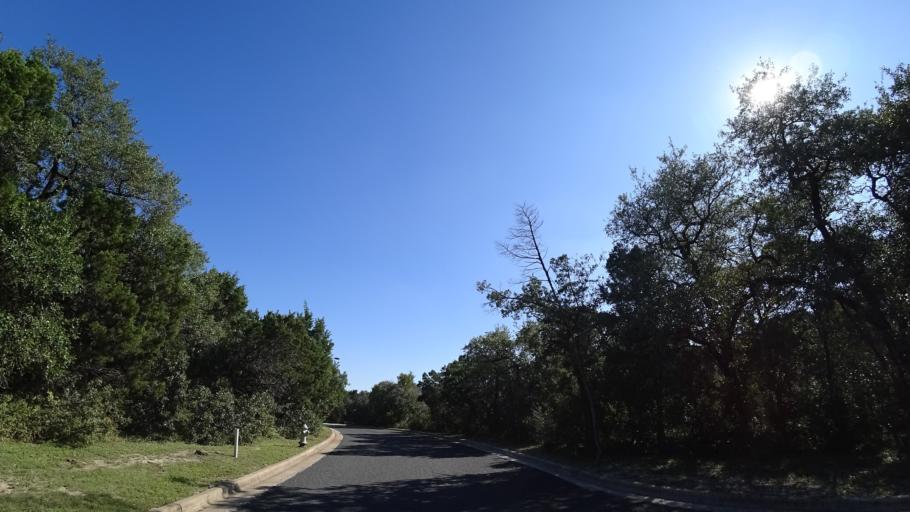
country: US
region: Texas
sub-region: Travis County
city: Rollingwood
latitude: 30.2493
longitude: -97.8015
